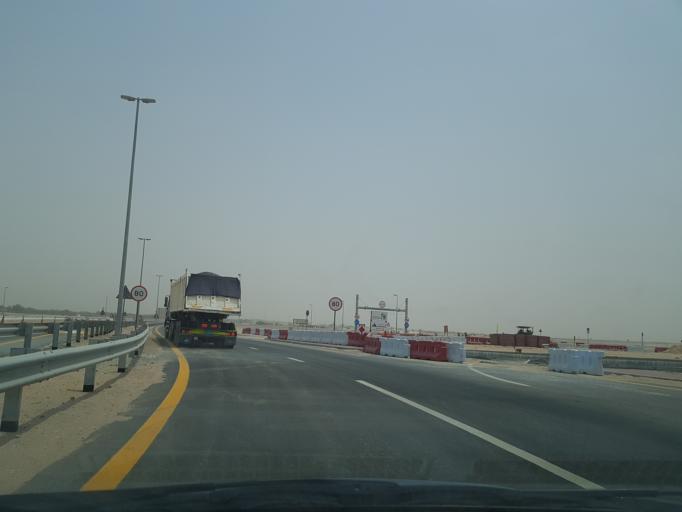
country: AE
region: Dubai
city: Dubai
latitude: 24.8505
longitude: 55.3463
